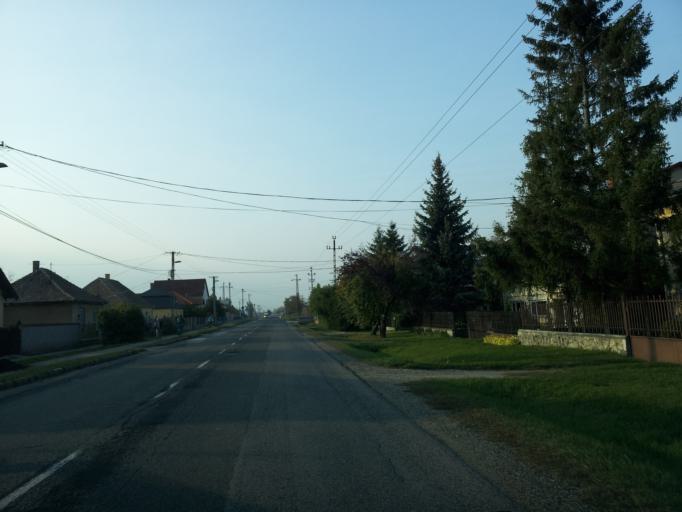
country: HU
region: Komarom-Esztergom
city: Kisber
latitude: 47.5061
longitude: 18.0172
